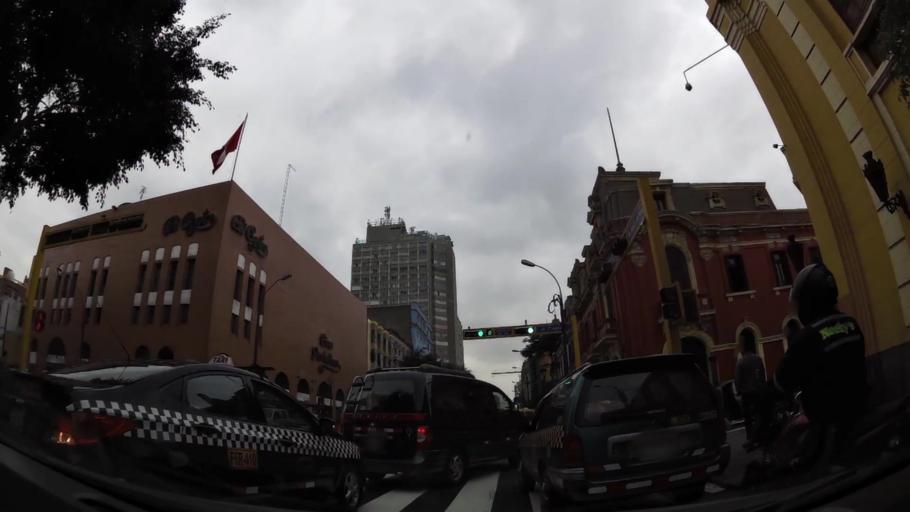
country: PE
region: Lima
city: Lima
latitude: -12.0481
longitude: -77.0401
